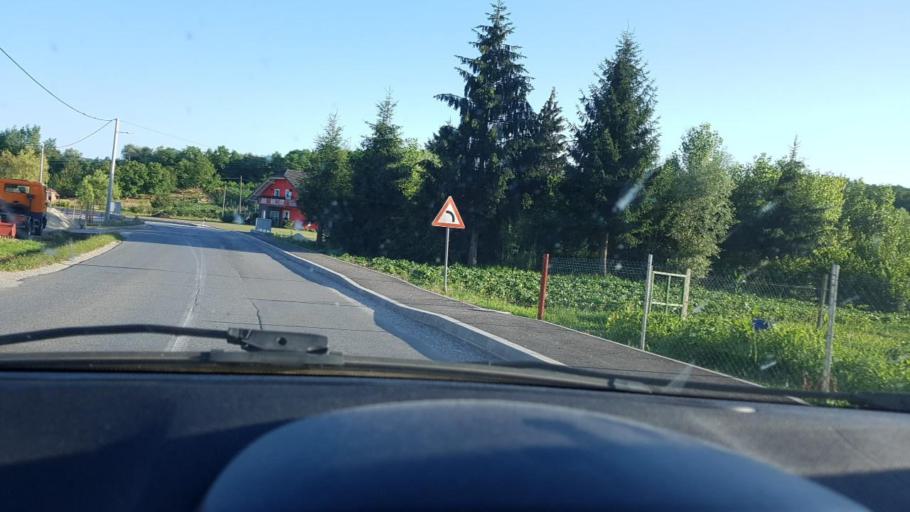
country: HR
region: Krapinsko-Zagorska
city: Bedekovcina
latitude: 46.0543
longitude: 16.0000
